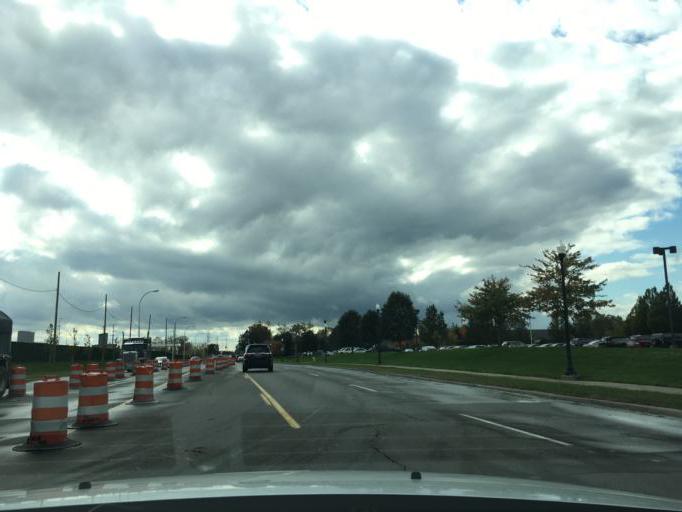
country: US
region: Michigan
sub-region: Wayne County
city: Dearborn
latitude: 42.3135
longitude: -83.1756
